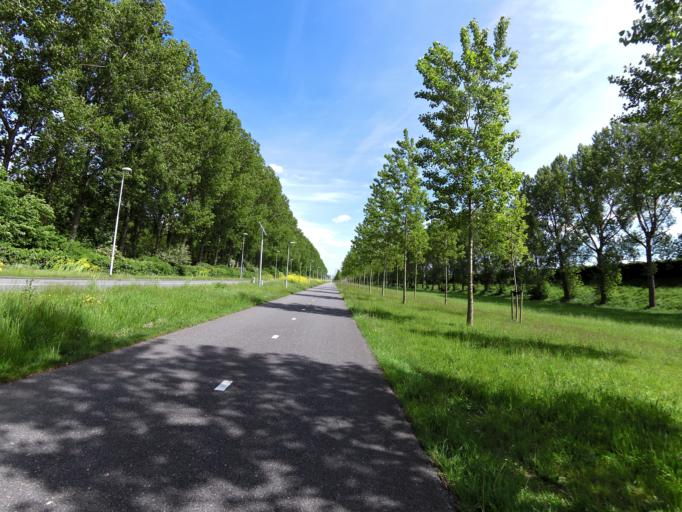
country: NL
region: South Holland
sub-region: Gemeente Maassluis
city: Maassluis
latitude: 51.9004
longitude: 4.2381
